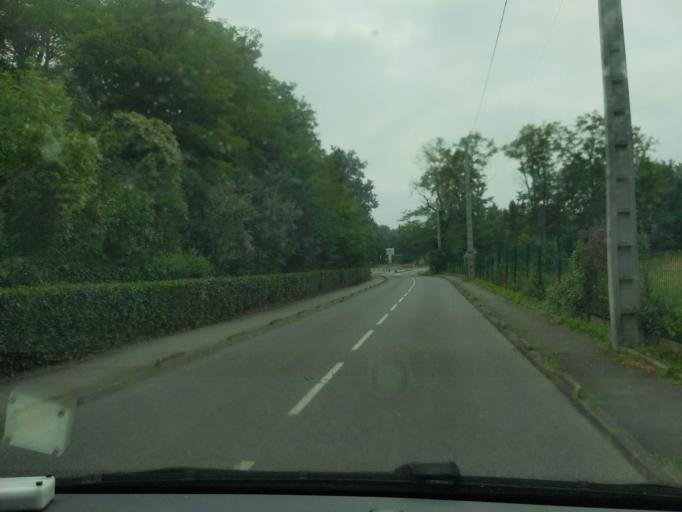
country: FR
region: Midi-Pyrenees
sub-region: Departement de la Haute-Garonne
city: Ramonville-Saint-Agne
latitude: 43.5562
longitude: 1.4570
